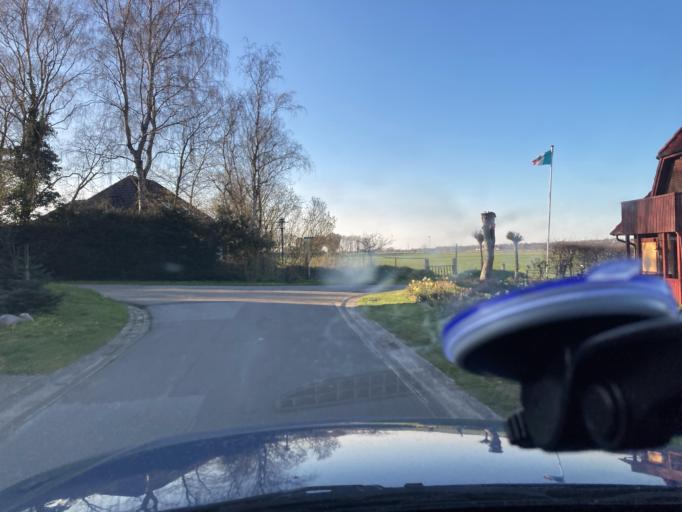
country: DE
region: Schleswig-Holstein
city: Ostrohe
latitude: 54.2155
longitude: 9.1396
